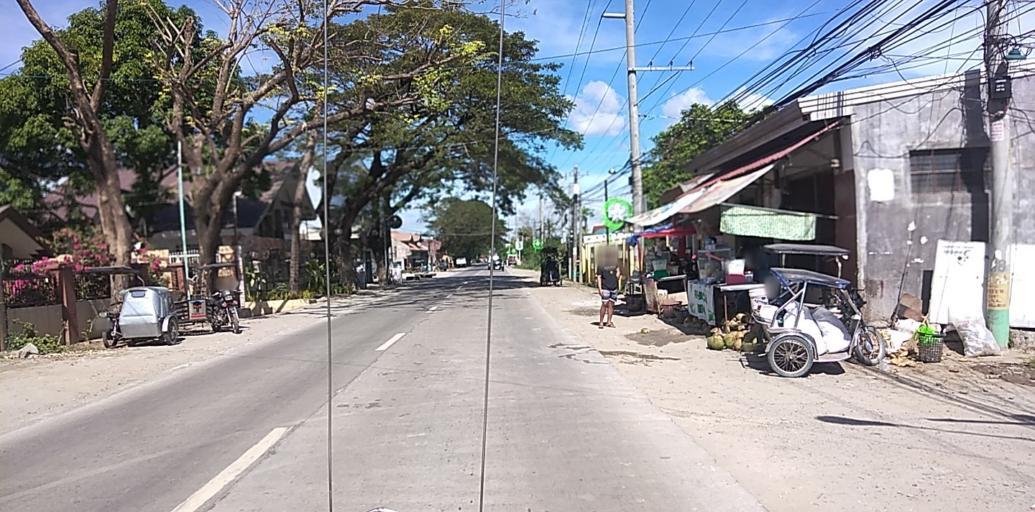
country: PH
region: Central Luzon
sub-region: Province of Pampanga
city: Santa Ana
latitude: 15.1209
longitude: 120.7758
